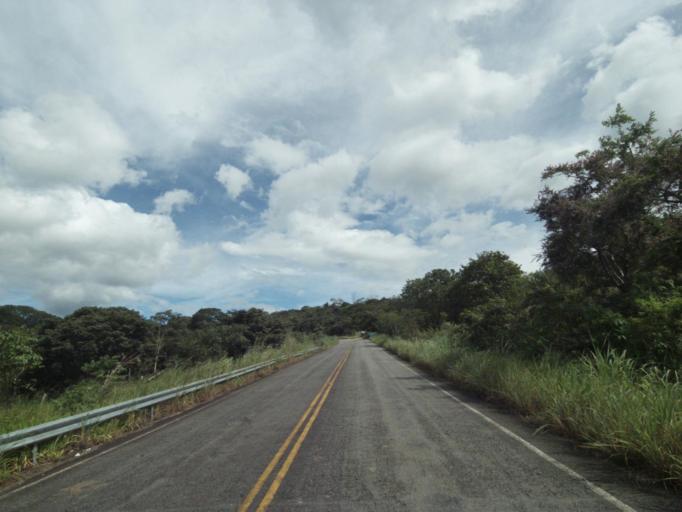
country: BR
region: Goias
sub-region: Pirenopolis
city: Pirenopolis
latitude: -15.7793
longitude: -49.0494
